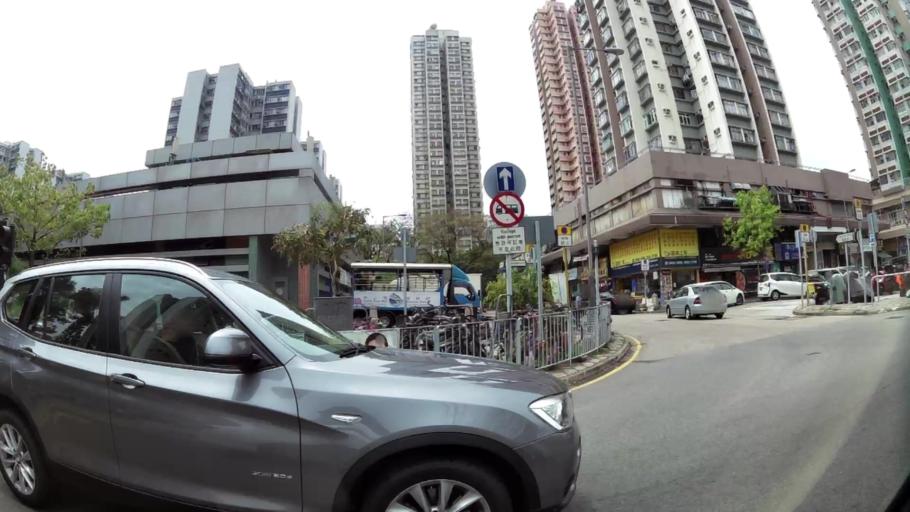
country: HK
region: Tuen Mun
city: Tuen Mun
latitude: 22.3883
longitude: 113.9805
